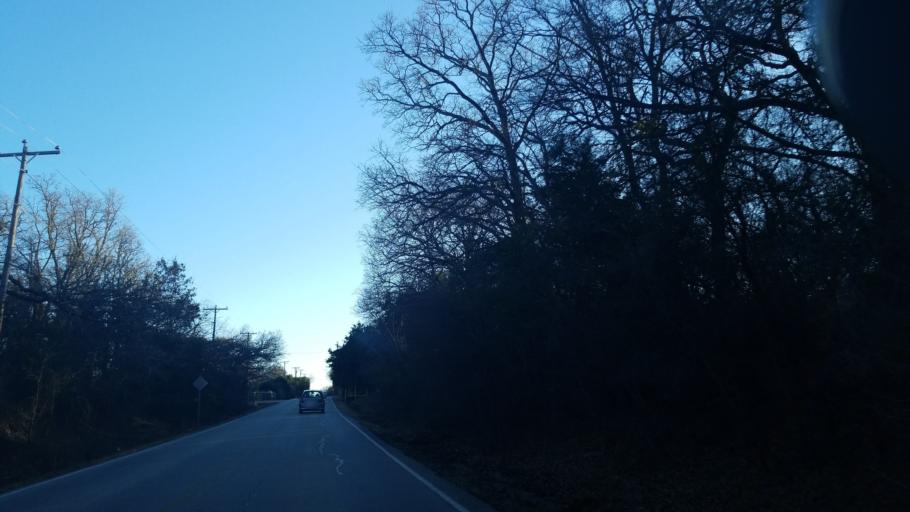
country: US
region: Texas
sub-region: Denton County
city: Shady Shores
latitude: 33.1475
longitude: -97.0299
